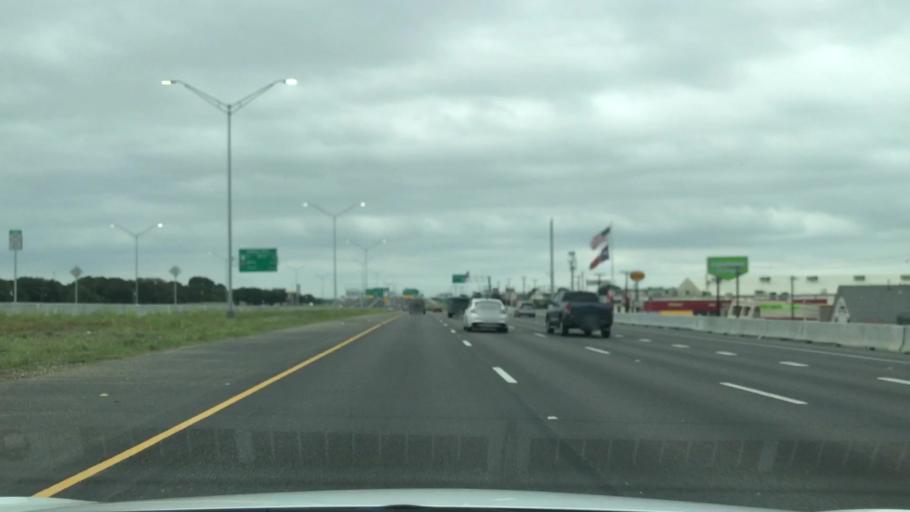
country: US
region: Texas
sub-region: Dallas County
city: Irving
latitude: 32.8369
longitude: -96.9505
